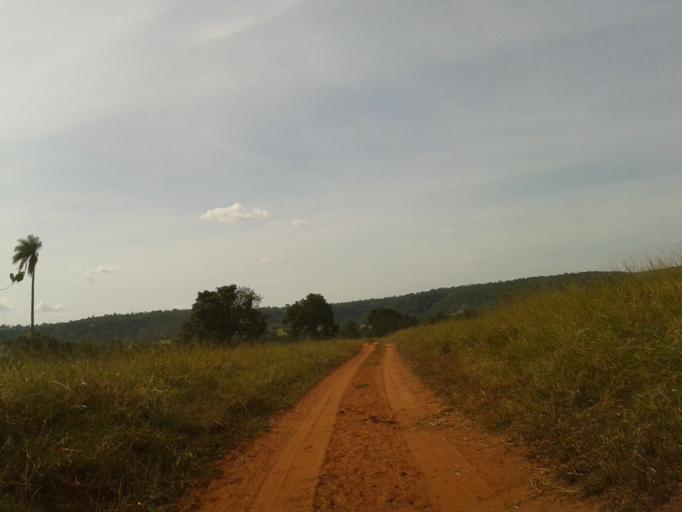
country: BR
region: Minas Gerais
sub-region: Campina Verde
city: Campina Verde
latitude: -19.5066
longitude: -49.5883
